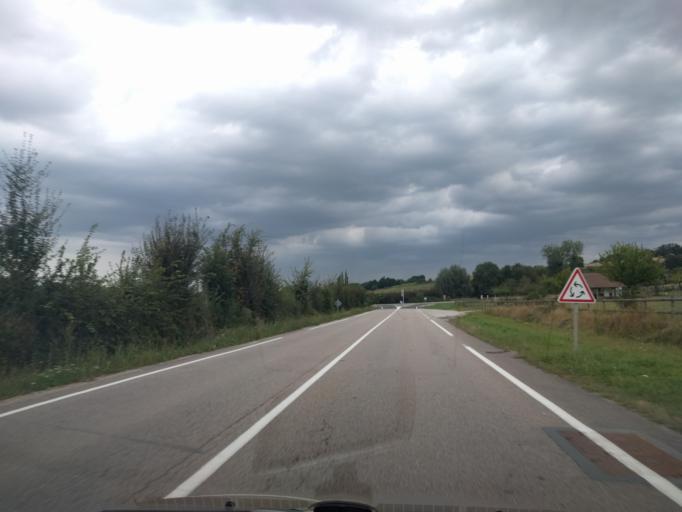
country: FR
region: Lower Normandy
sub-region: Departement de l'Orne
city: Gace
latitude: 48.7765
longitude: 0.3023
